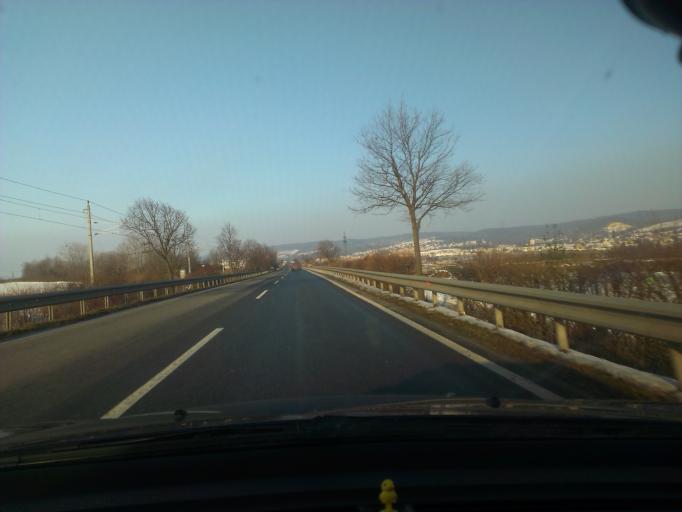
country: AT
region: Burgenland
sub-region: Eisenstadt-Umgebung
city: Trausdorf an der Wulka
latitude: 47.8438
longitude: 16.5606
